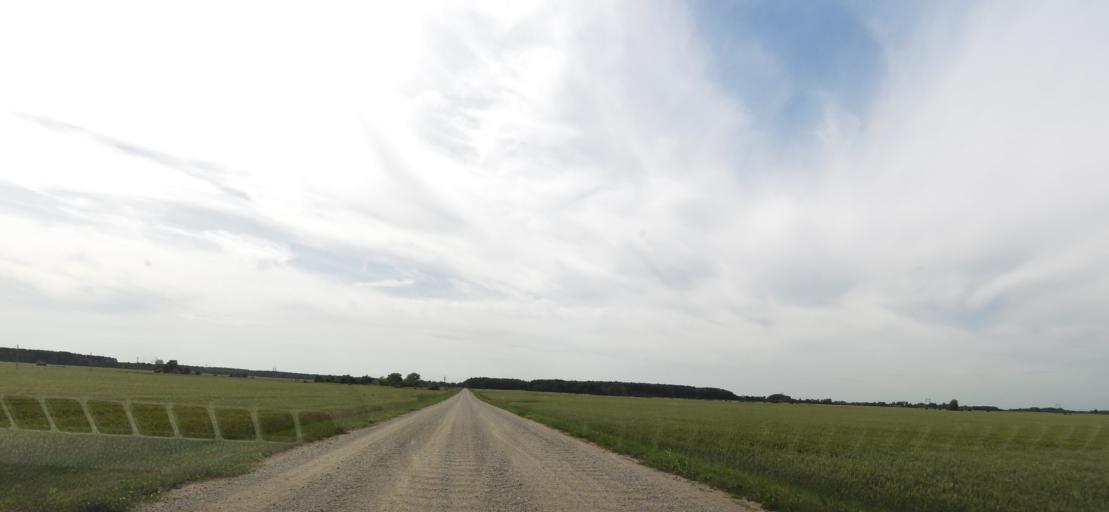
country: LT
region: Panevezys
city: Pasvalys
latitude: 55.9653
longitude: 24.3314
